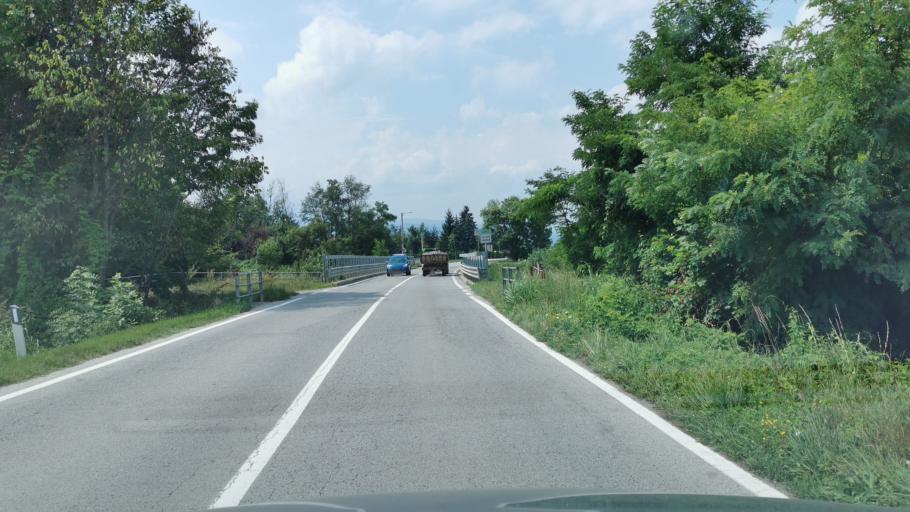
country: IT
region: Piedmont
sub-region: Provincia di Cuneo
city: Roata Rossi
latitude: 44.4356
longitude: 7.4992
